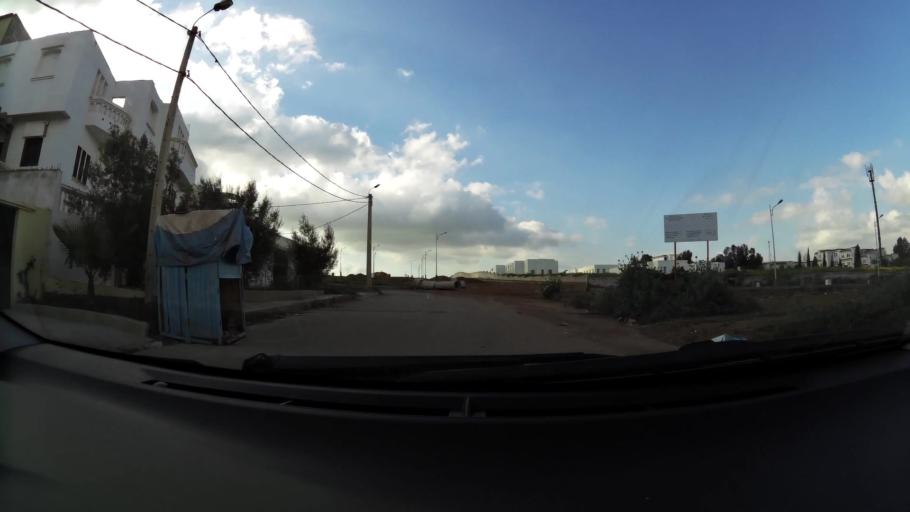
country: MA
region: Chaouia-Ouardigha
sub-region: Settat Province
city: Settat
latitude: 33.0091
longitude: -7.6376
